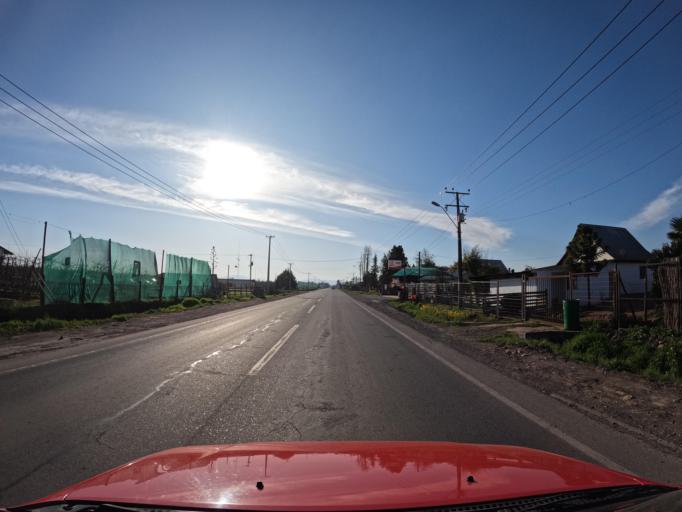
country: CL
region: Maule
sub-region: Provincia de Curico
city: Teno
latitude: -34.8961
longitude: -71.0618
